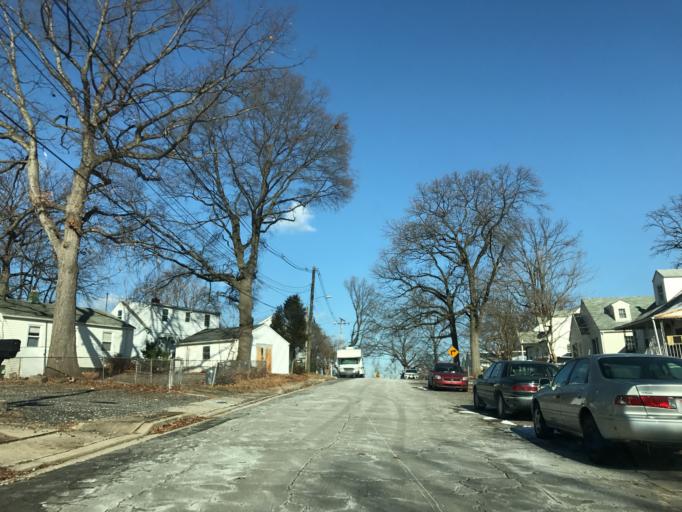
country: US
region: Maryland
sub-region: Baltimore County
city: Middle River
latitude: 39.3219
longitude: -76.4500
